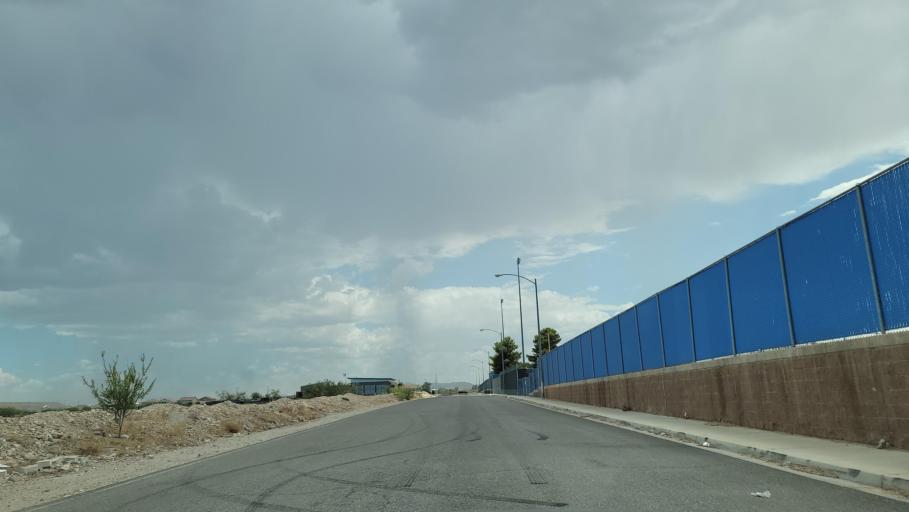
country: US
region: Nevada
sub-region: Clark County
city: Enterprise
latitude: 36.0515
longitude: -115.2656
